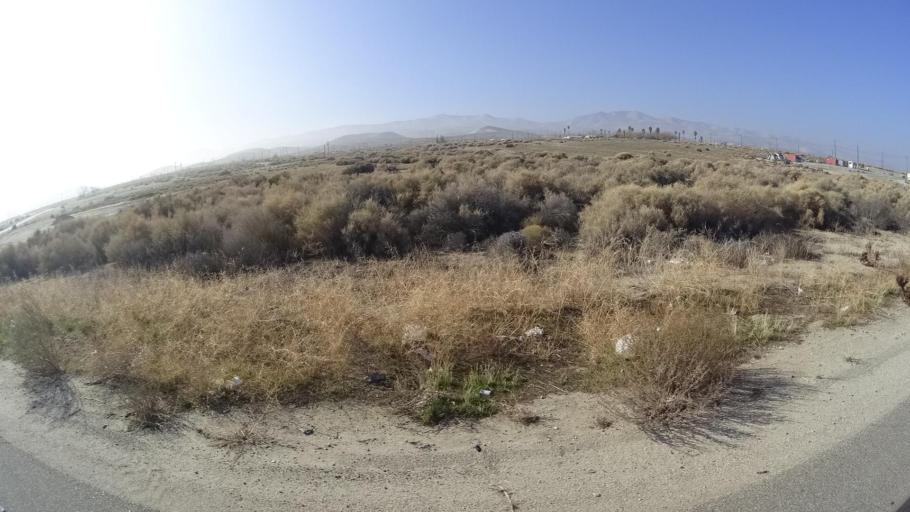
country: US
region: California
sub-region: Kern County
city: Taft Heights
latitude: 35.1845
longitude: -119.5508
